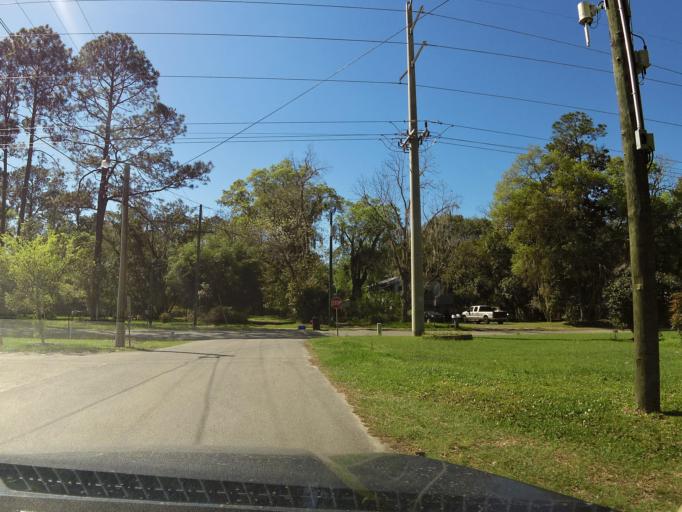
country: US
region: Florida
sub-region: Bradford County
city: Starke
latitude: 29.9367
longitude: -82.1019
